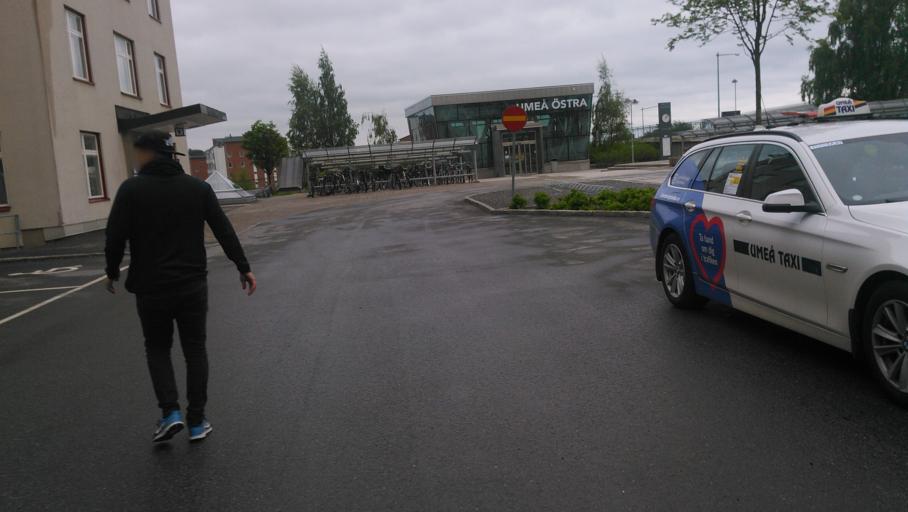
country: SE
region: Vaesterbotten
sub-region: Umea Kommun
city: Umea
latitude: 63.8174
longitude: 20.2968
